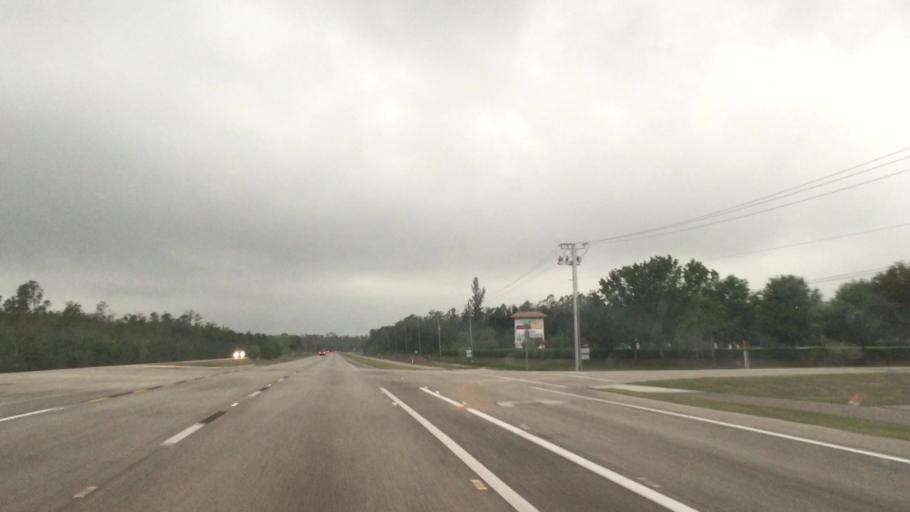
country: US
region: Florida
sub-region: Lee County
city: Villas
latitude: 26.5652
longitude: -81.8302
